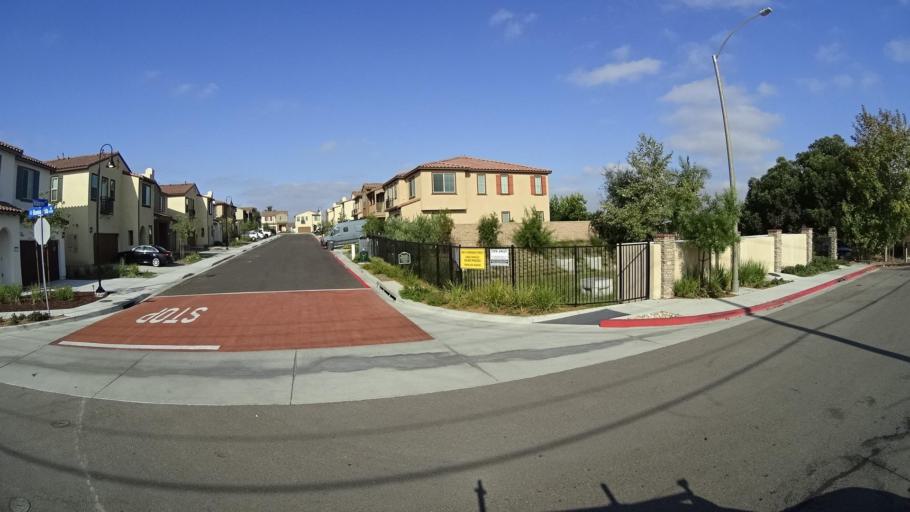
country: US
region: California
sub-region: San Diego County
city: Vista
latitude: 33.1700
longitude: -117.2464
